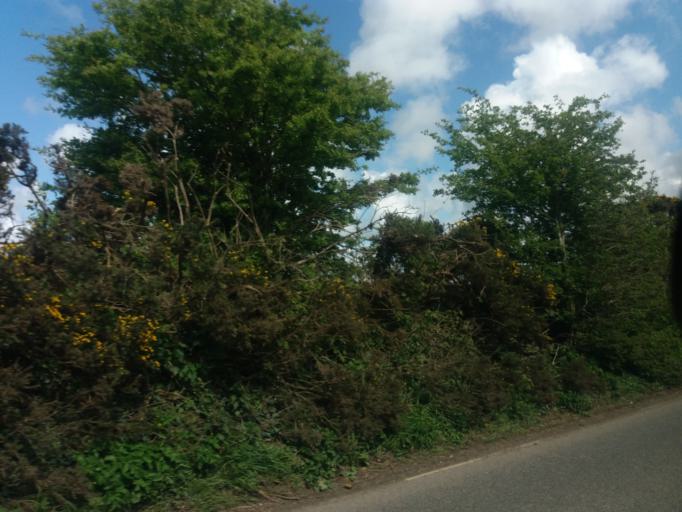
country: IE
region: Leinster
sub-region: Loch Garman
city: New Ross
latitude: 52.2610
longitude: -6.7966
